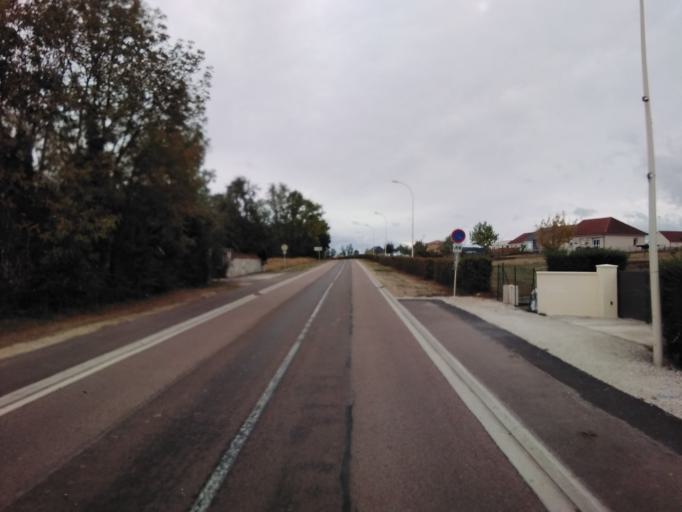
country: FR
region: Champagne-Ardenne
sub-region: Departement de l'Aube
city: Vendeuvre-sur-Barse
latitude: 48.2310
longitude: 4.4595
